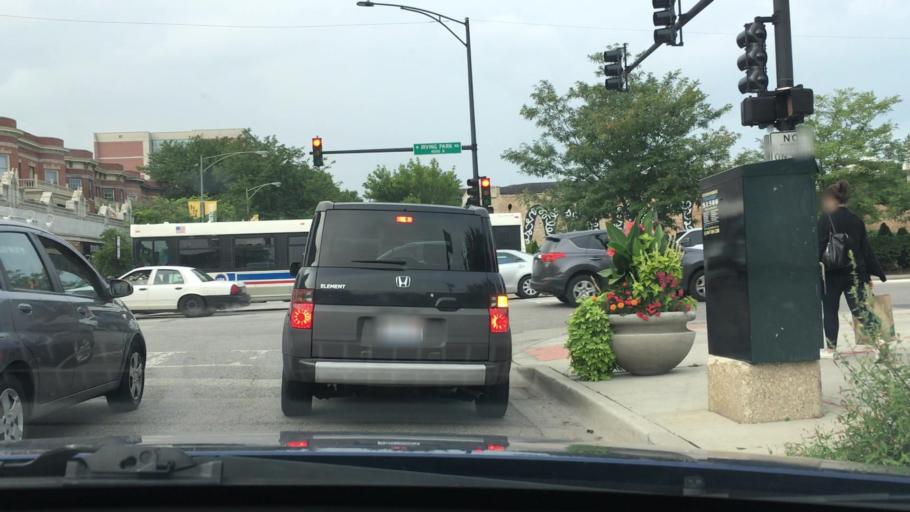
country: US
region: Illinois
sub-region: Cook County
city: Lincolnwood
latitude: 41.9543
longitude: -87.6545
